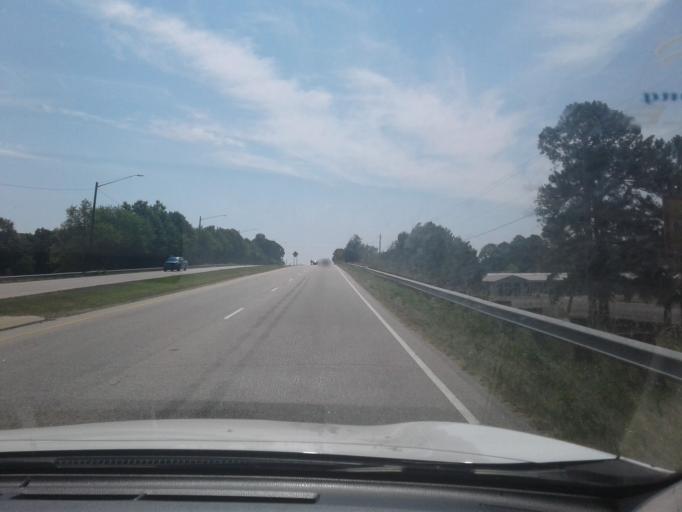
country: US
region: North Carolina
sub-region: Harnett County
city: Erwin
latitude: 35.3307
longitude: -78.6654
